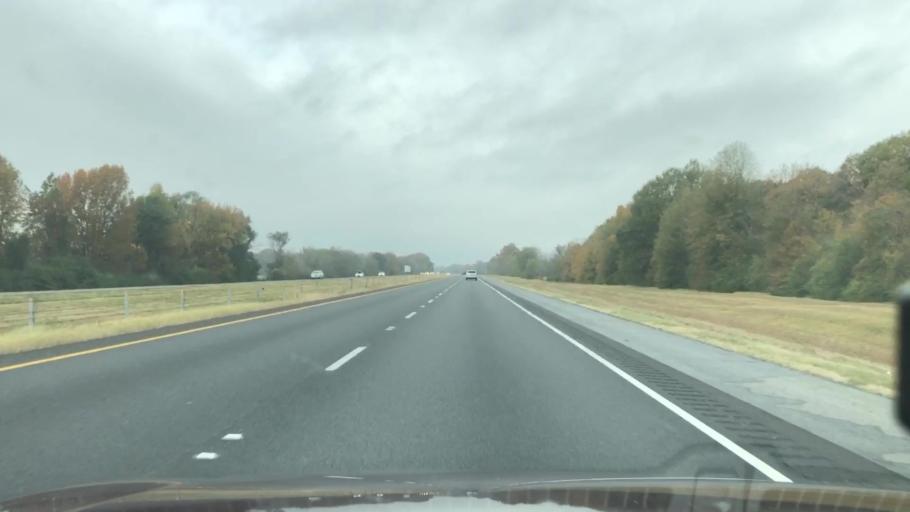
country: US
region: Louisiana
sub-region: Richland Parish
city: Rayville
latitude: 32.4630
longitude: -91.7885
